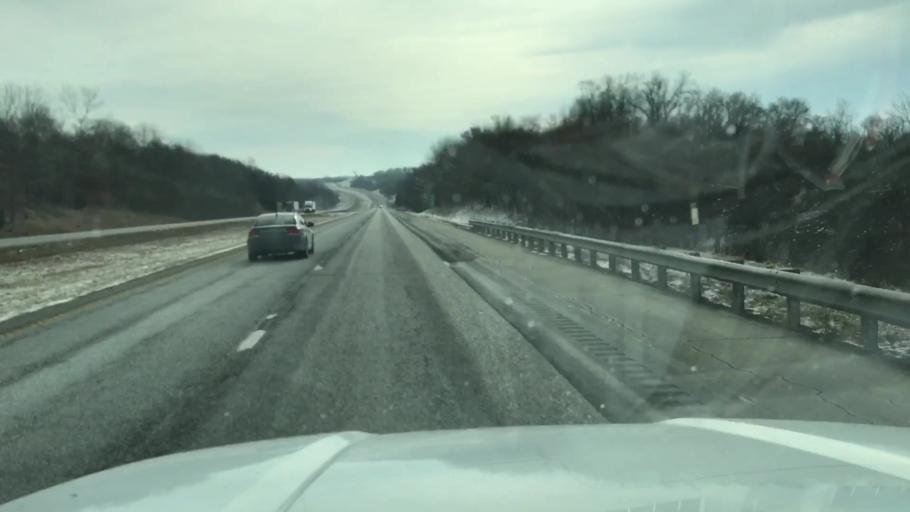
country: US
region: Missouri
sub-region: Holt County
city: Oregon
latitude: 39.9815
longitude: -95.0300
